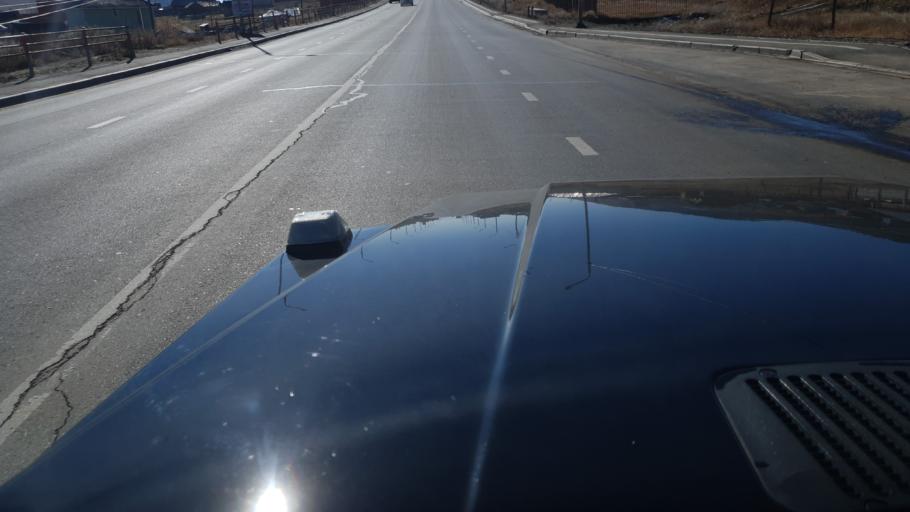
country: MN
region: Ulaanbaatar
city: Ulaanbaatar
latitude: 48.0430
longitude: 106.9032
